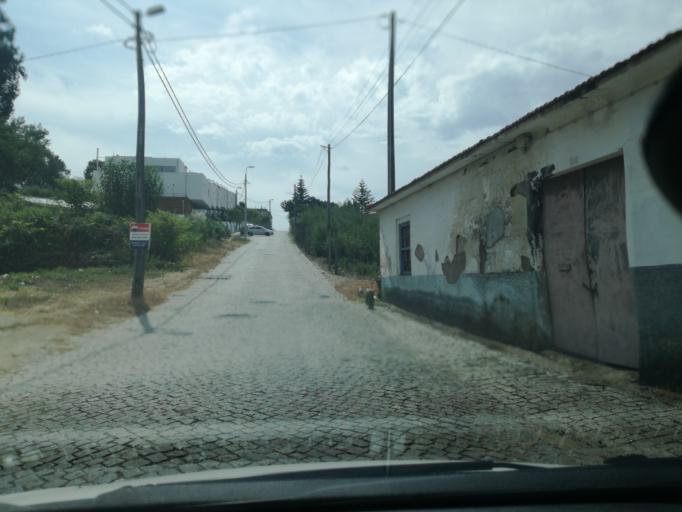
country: PT
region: Porto
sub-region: Vila Nova de Gaia
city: Grijo
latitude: 41.0203
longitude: -8.5859
